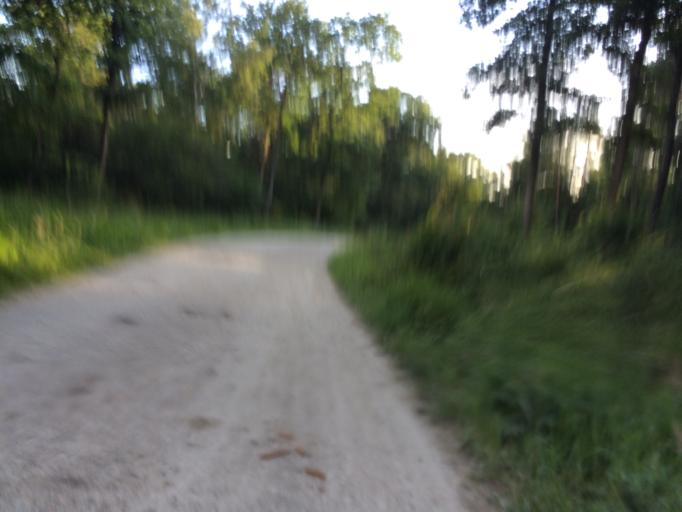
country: FR
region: Ile-de-France
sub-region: Departement de l'Essonne
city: Soisy-sur-Seine
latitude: 48.6642
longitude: 2.4734
